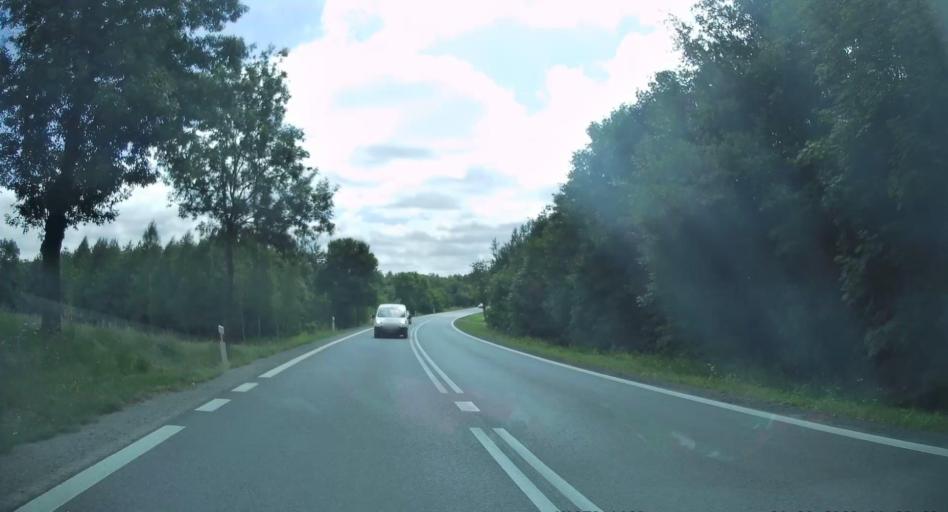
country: PL
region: Swietokrzyskie
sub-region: Powiat sandomierski
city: Klimontow
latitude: 50.6296
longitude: 21.4750
